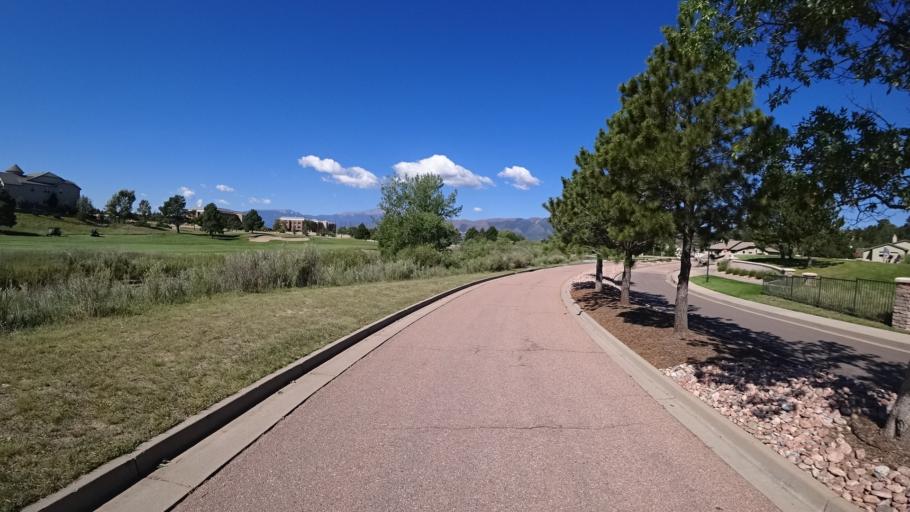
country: US
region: Colorado
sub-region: El Paso County
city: Air Force Academy
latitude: 38.9711
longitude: -104.7838
